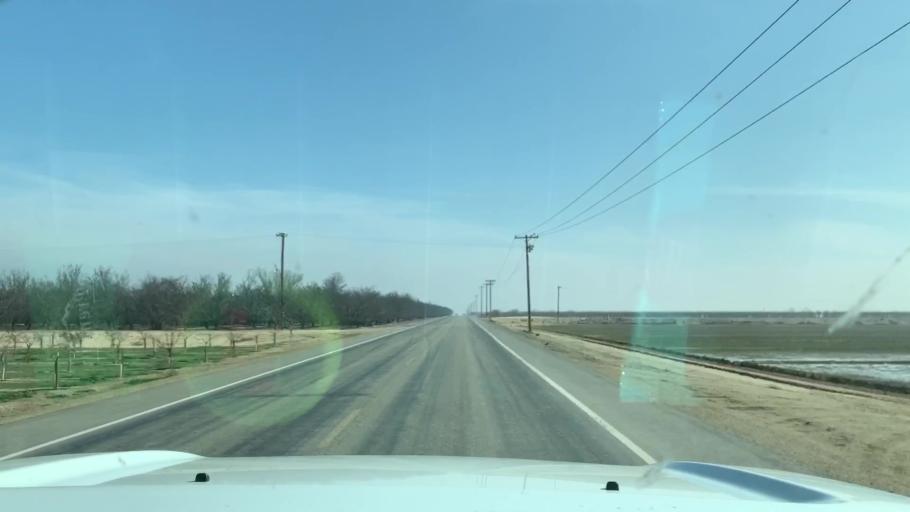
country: US
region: California
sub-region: Kern County
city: Buttonwillow
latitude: 35.4424
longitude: -119.4846
